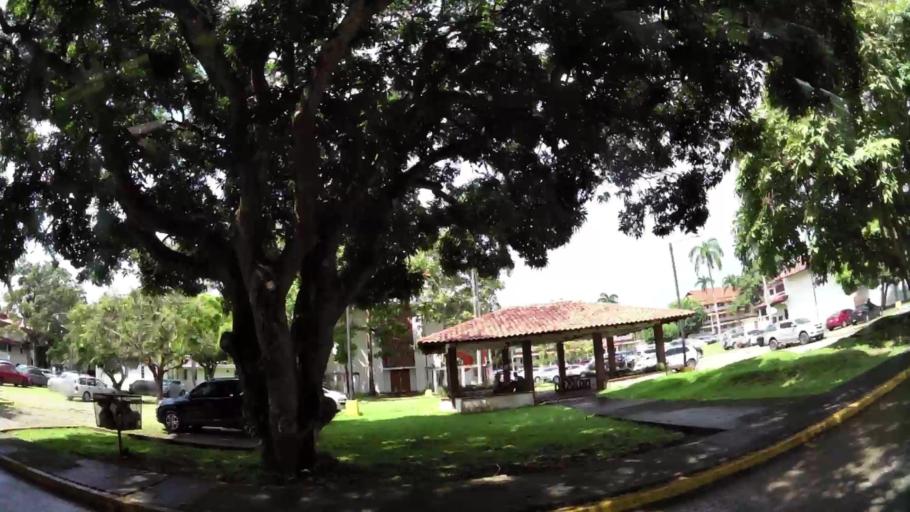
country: PA
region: Panama
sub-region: Distrito de Panama
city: Ancon
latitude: 8.9979
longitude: -79.5828
